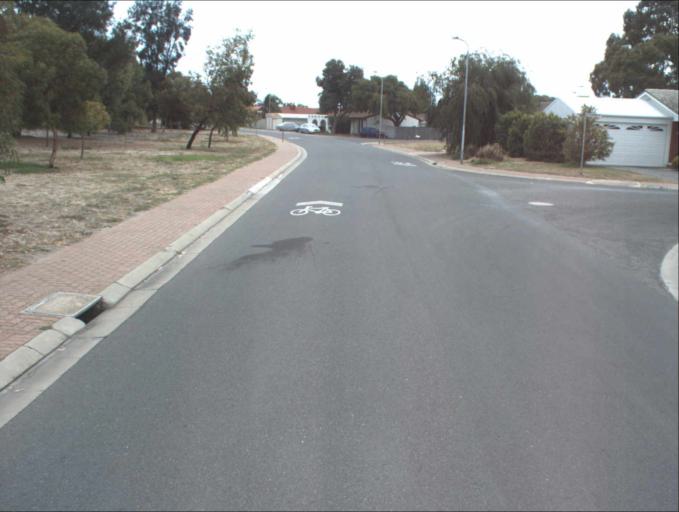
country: AU
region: South Australia
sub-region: Port Adelaide Enfield
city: Birkenhead
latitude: -34.7885
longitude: 138.4989
